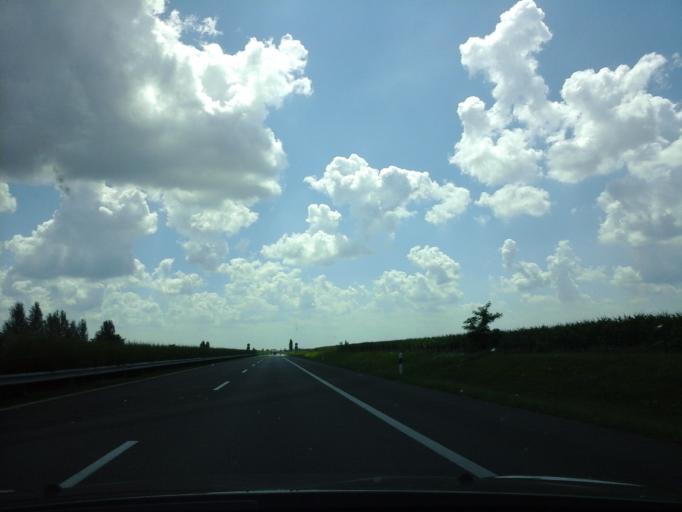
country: HU
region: Hajdu-Bihar
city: Ebes
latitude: 47.5119
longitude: 21.5488
